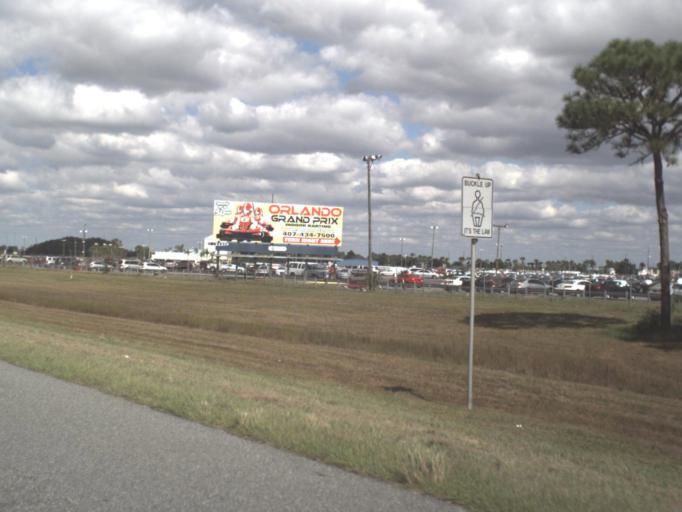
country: US
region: Florida
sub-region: Orange County
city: Taft
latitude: 28.4228
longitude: -81.3948
